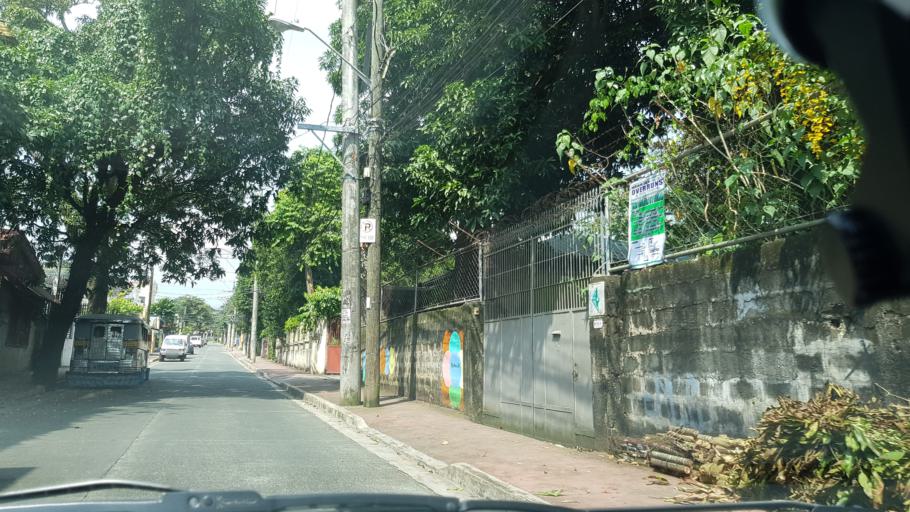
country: PH
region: Calabarzon
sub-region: Province of Rizal
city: Antipolo
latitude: 14.6493
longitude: 121.1192
